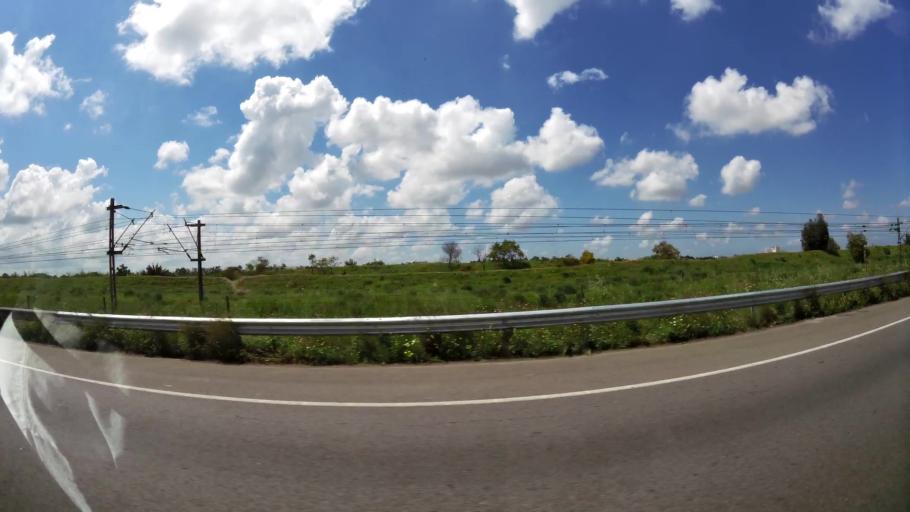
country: MA
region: Grand Casablanca
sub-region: Nouaceur
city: Bouskoura
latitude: 33.4278
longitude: -7.6277
